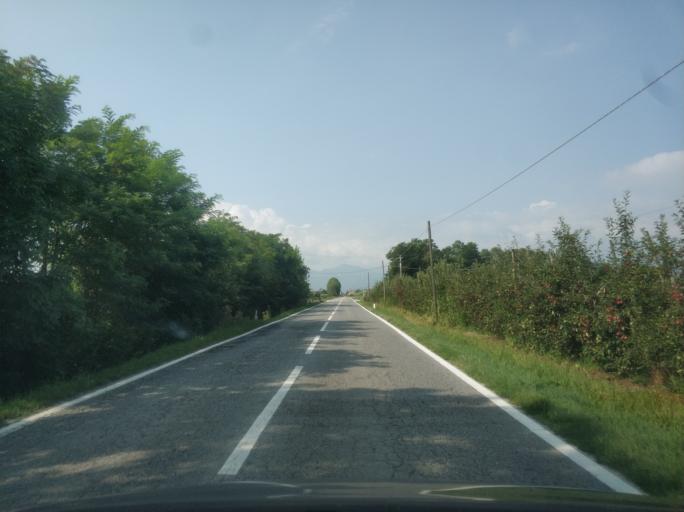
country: IT
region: Piedmont
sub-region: Provincia di Cuneo
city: Roata Rossi
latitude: 44.4649
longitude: 7.5012
